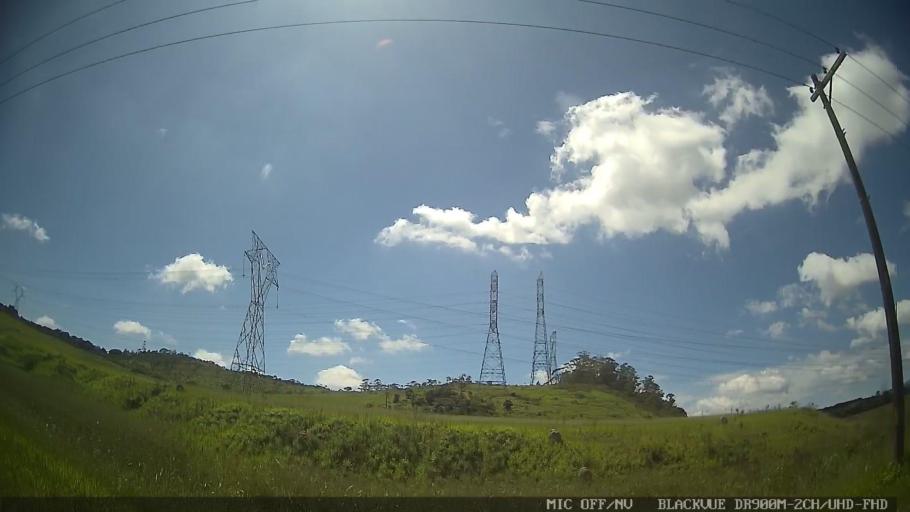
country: BR
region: Sao Paulo
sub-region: Mogi das Cruzes
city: Mogi das Cruzes
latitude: -23.6207
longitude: -46.2012
